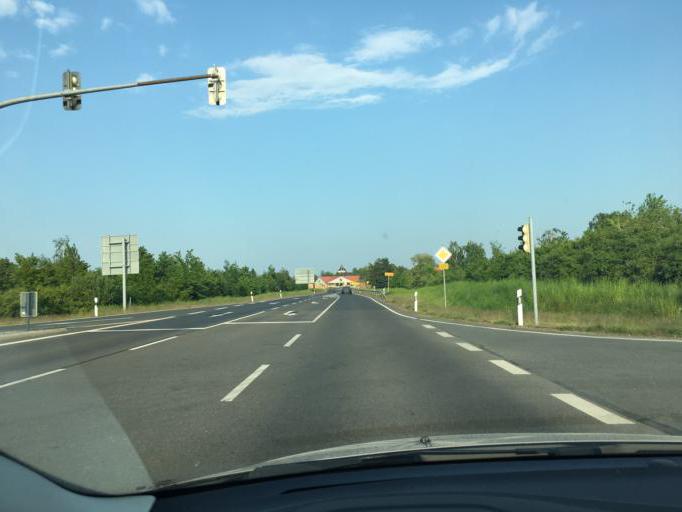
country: DE
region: Saxony
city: Grimma
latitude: 51.2520
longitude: 12.7201
